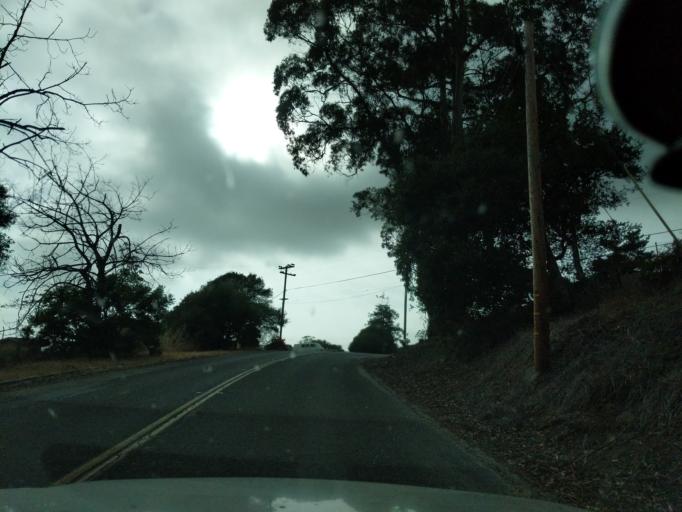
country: US
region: California
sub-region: Monterey County
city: Elkhorn
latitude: 36.8098
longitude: -121.7212
